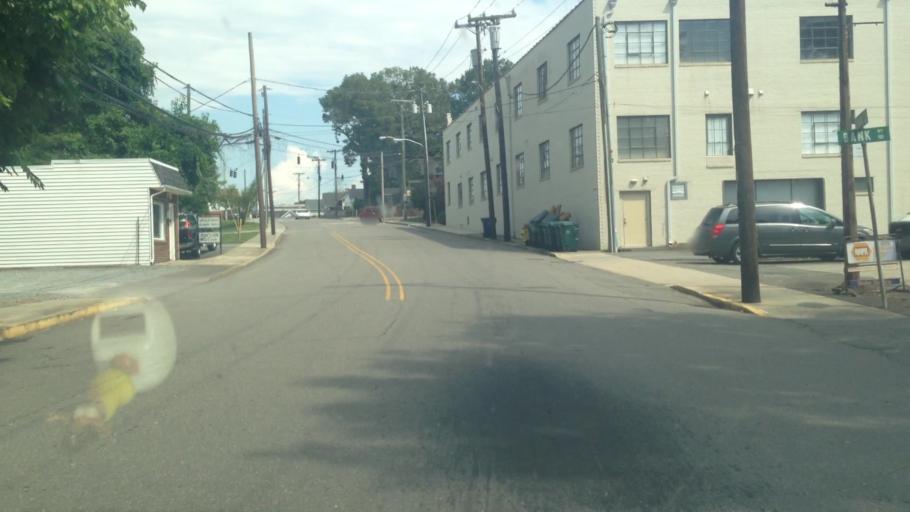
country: US
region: North Carolina
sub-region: Surry County
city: Mount Airy
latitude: 36.4952
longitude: -80.6021
